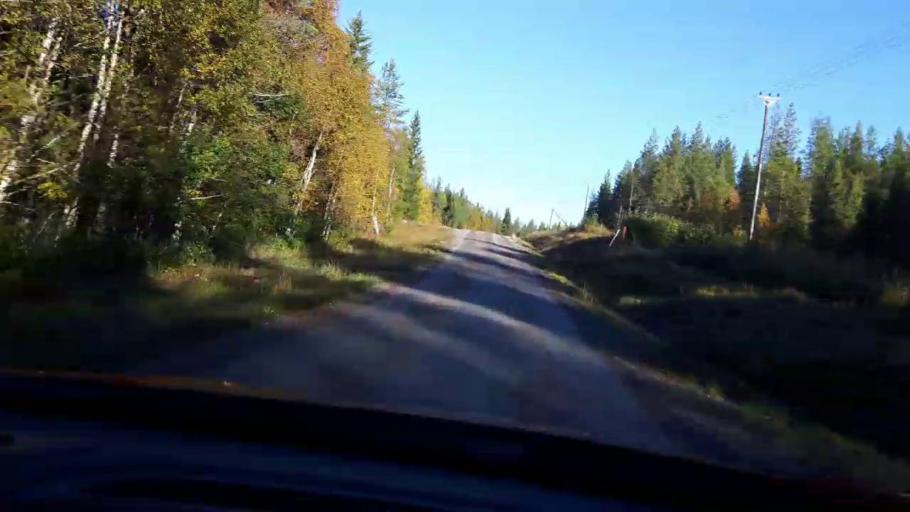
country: SE
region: Jaemtland
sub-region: Stroemsunds Kommun
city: Stroemsund
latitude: 64.3725
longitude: 15.1548
